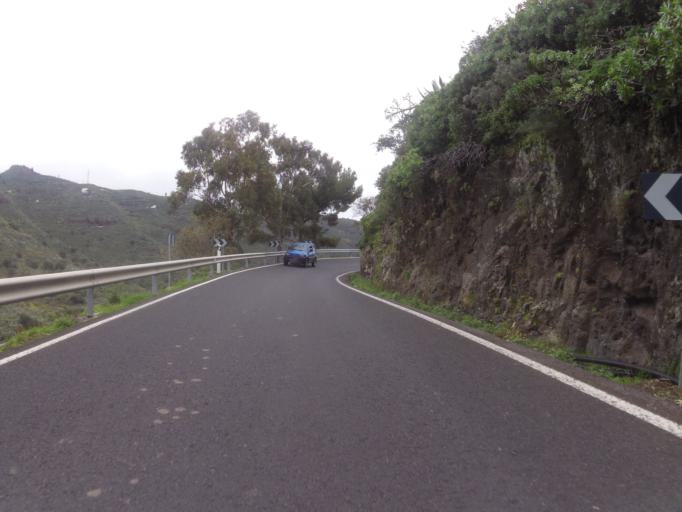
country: ES
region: Canary Islands
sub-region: Provincia de Las Palmas
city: Vega de San Mateo
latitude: 27.9941
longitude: -15.5283
